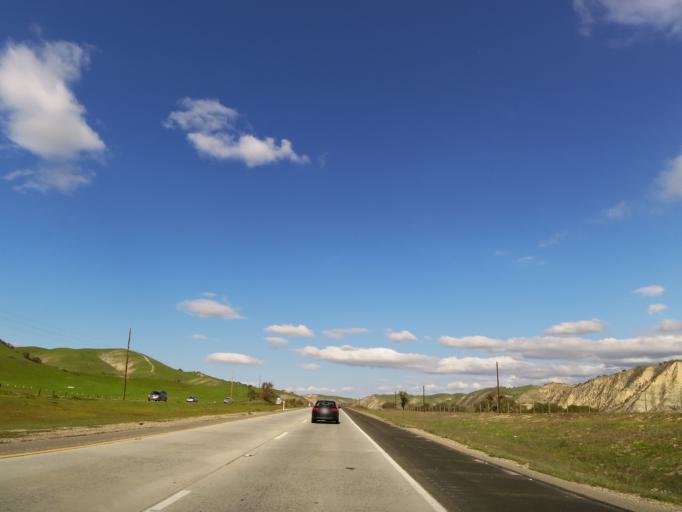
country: US
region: California
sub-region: San Luis Obispo County
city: Lake Nacimiento
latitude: 35.8859
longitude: -120.8417
